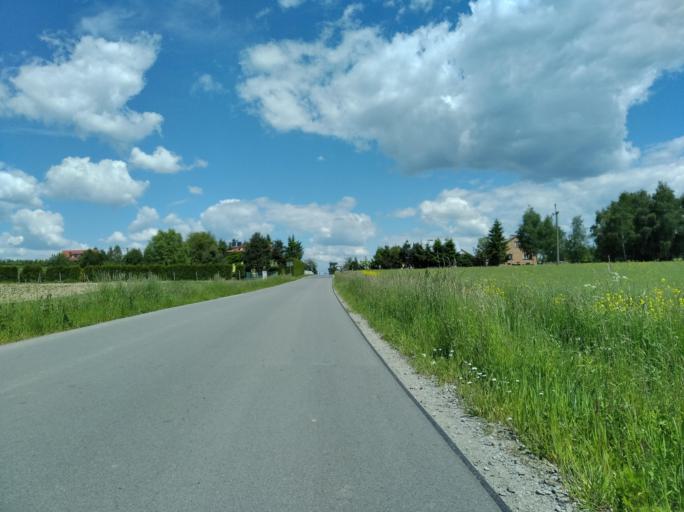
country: PL
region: Subcarpathian Voivodeship
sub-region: Powiat jasielski
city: Tarnowiec
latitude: 49.7745
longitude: 21.6112
